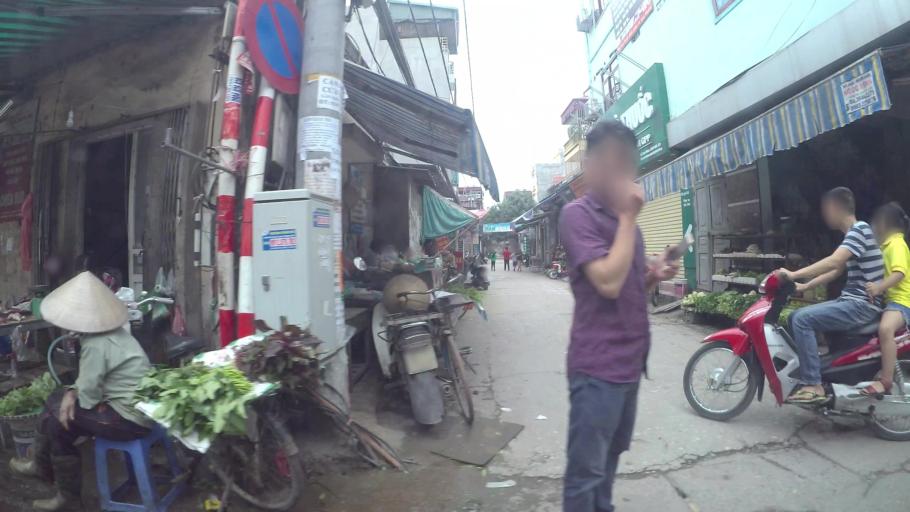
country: VN
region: Ha Noi
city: Hai BaTrung
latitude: 20.9842
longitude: 105.8874
